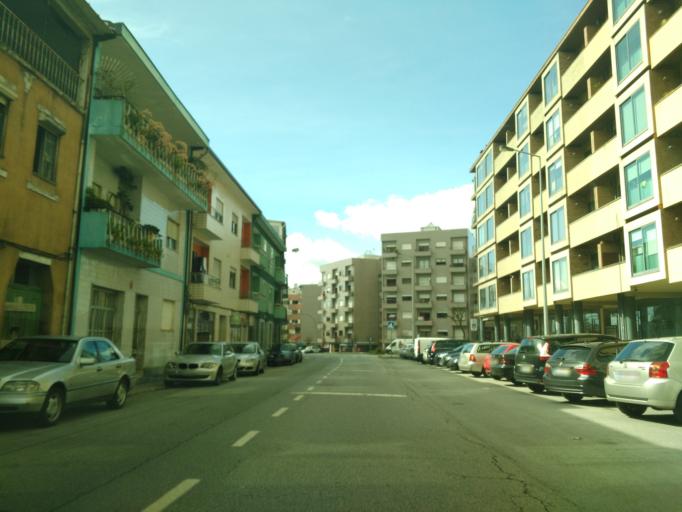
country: PT
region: Braga
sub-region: Braga
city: Braga
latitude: 41.5414
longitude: -8.4135
